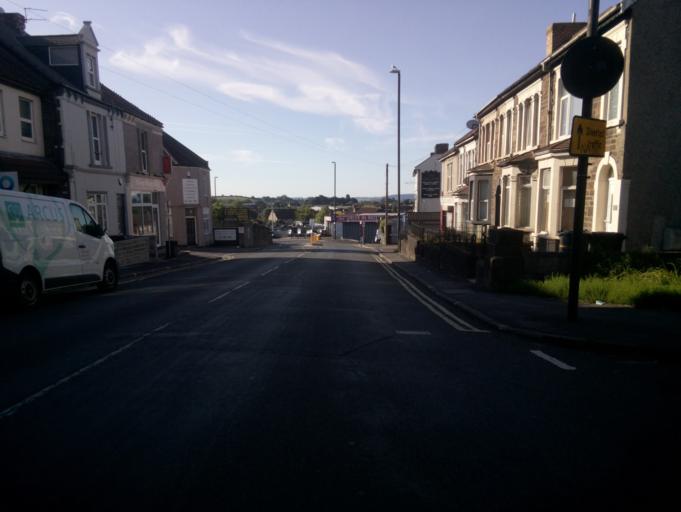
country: GB
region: England
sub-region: South Gloucestershire
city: Kingswood
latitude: 51.4527
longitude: -2.5239
